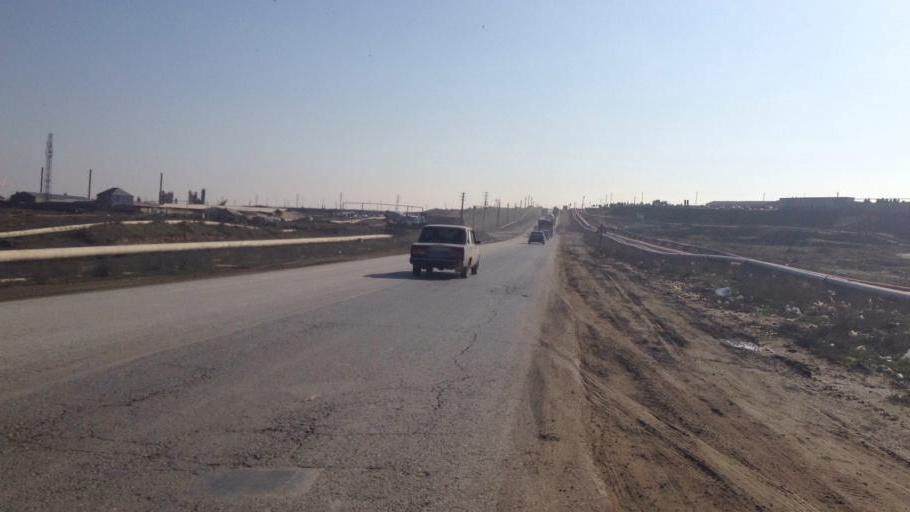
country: AZ
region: Abseron
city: Digah
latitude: 40.4675
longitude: 49.8865
